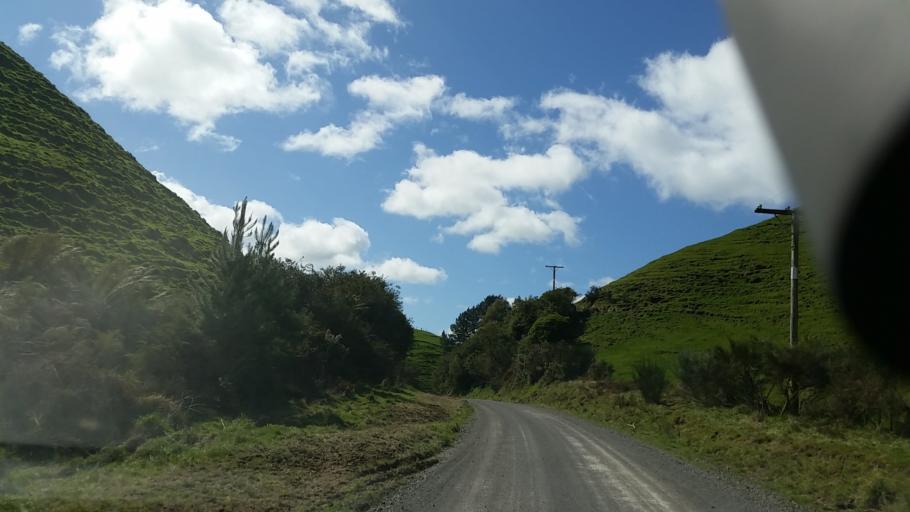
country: NZ
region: Waikato
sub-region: Taupo District
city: Taupo
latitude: -38.4778
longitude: 176.2180
